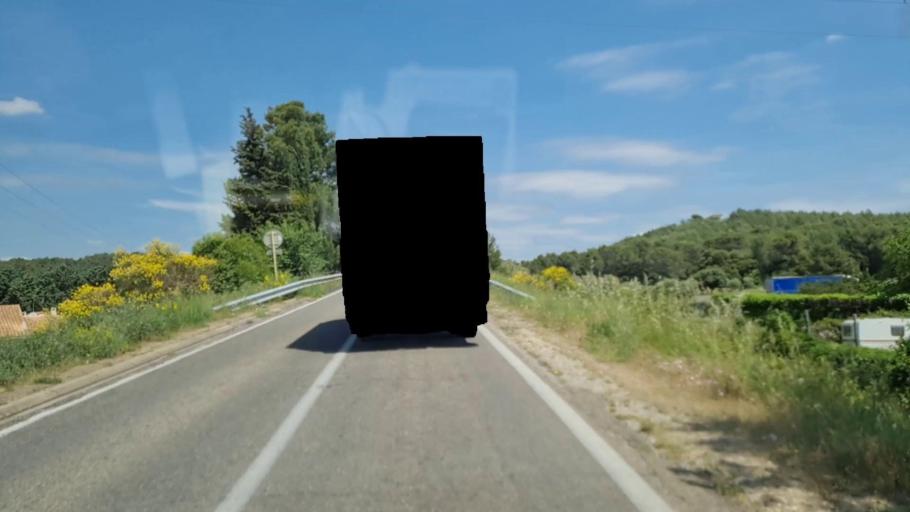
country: FR
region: Languedoc-Roussillon
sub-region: Departement du Gard
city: Saint-Gervasy
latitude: 43.8793
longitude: 4.4685
